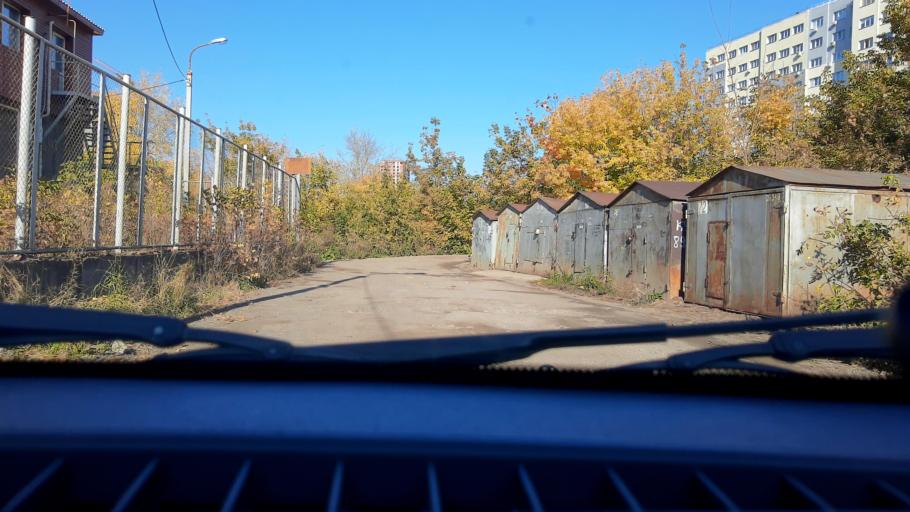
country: RU
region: Bashkortostan
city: Ufa
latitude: 54.7439
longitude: 55.9621
